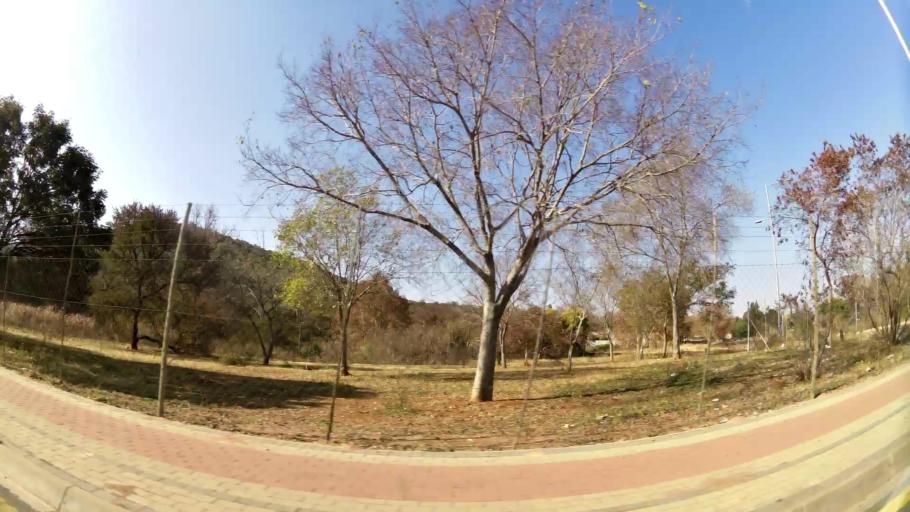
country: ZA
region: Gauteng
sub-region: City of Tshwane Metropolitan Municipality
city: Pretoria
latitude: -25.6987
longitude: 28.1877
